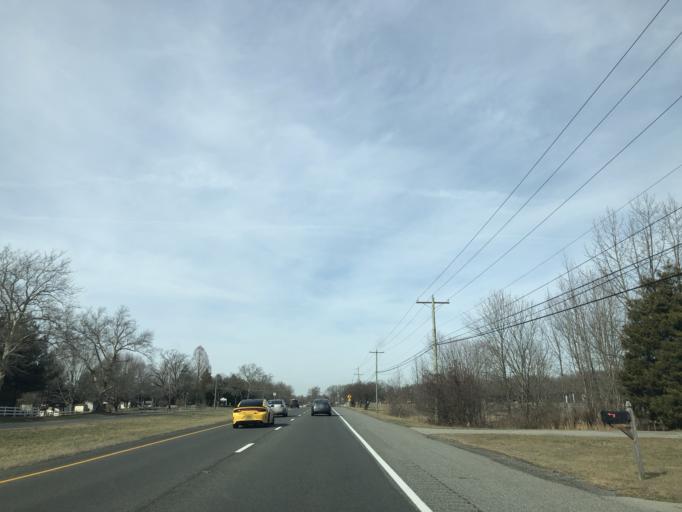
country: US
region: Delaware
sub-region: New Castle County
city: Townsend
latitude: 39.3545
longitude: -75.6436
